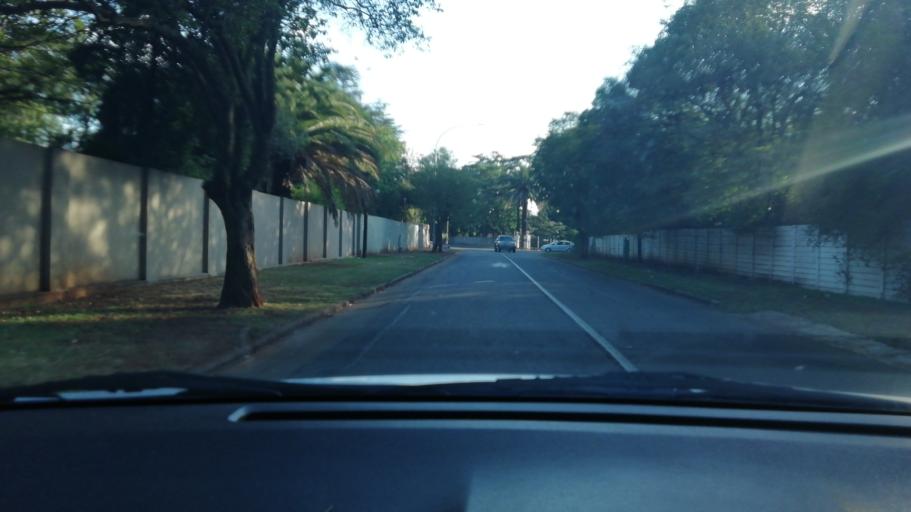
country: ZA
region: Gauteng
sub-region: Ekurhuleni Metropolitan Municipality
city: Benoni
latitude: -26.1996
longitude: 28.2973
